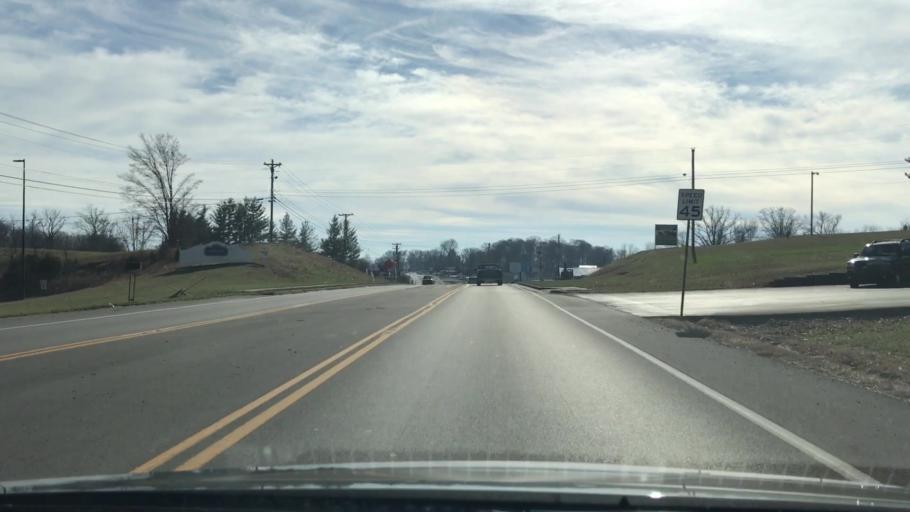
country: US
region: Kentucky
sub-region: Monroe County
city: Tompkinsville
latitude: 36.7237
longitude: -85.6875
